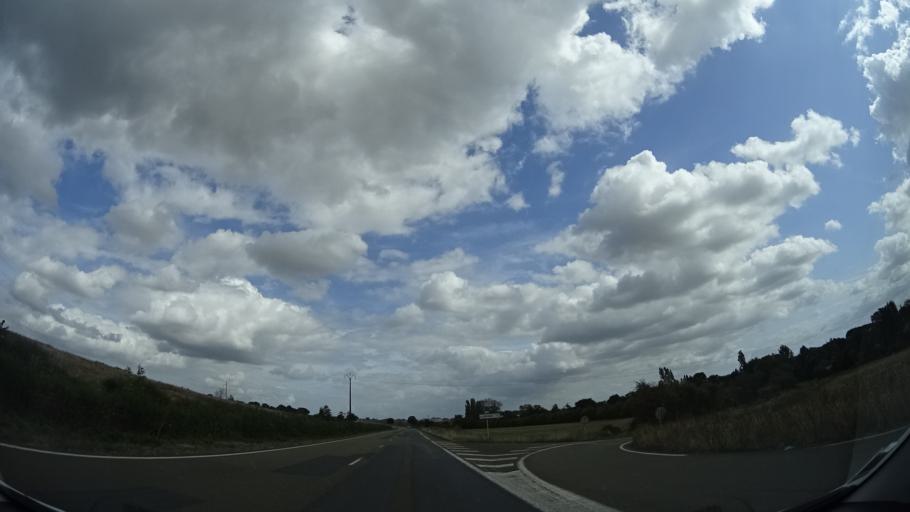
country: FR
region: Pays de la Loire
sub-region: Departement de la Mayenne
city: Argentre
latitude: 48.0655
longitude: -0.6402
